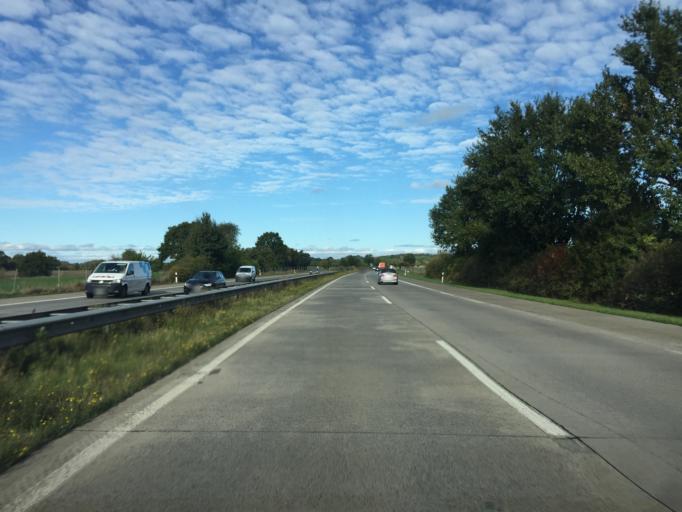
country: DE
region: Schleswig-Holstein
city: Ratekau
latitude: 53.9659
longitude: 10.7368
